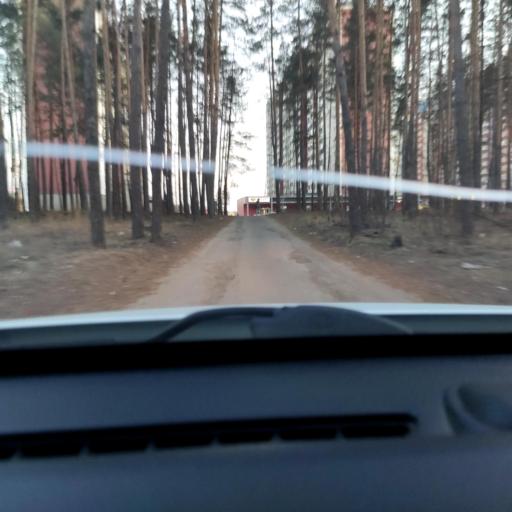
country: RU
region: Voronezj
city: Somovo
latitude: 51.7430
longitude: 39.3166
